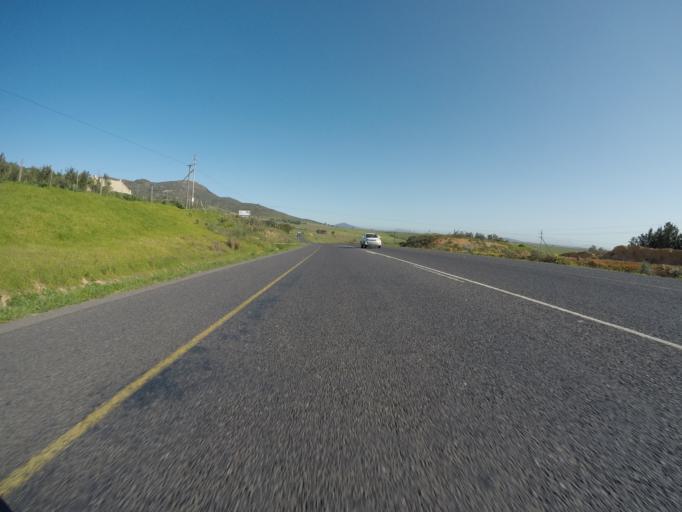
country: ZA
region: Western Cape
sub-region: Cape Winelands District Municipality
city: Noorder-Paarl
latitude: -33.6814
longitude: 18.9014
